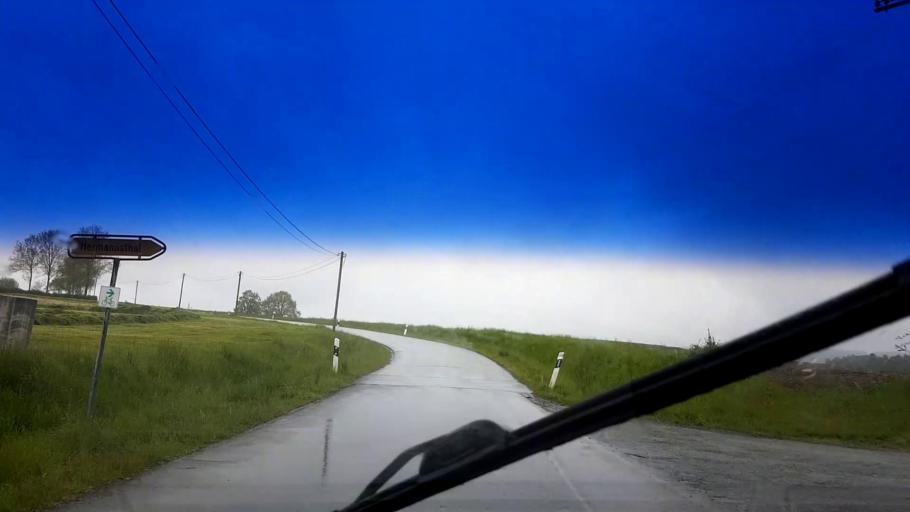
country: DE
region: Bavaria
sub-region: Upper Franconia
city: Bindlach
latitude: 50.0183
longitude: 11.6277
